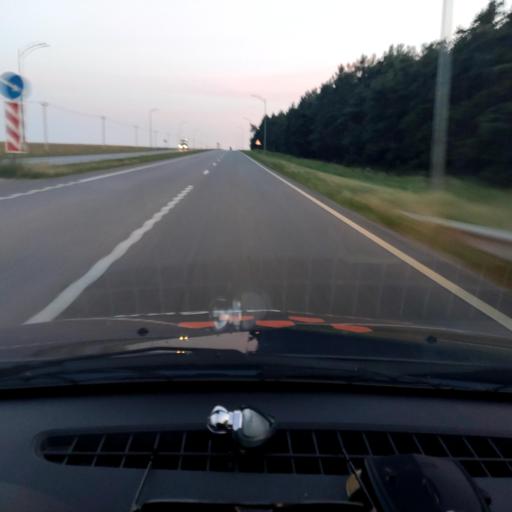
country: RU
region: Belgorod
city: Staryy Oskol
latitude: 51.4016
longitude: 37.8762
